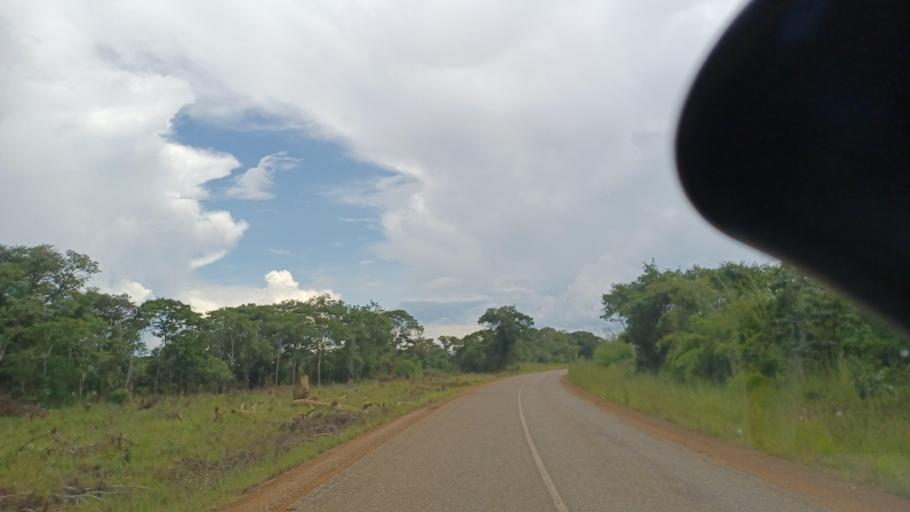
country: ZM
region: North-Western
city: Kasempa
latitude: -13.1320
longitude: 25.8767
